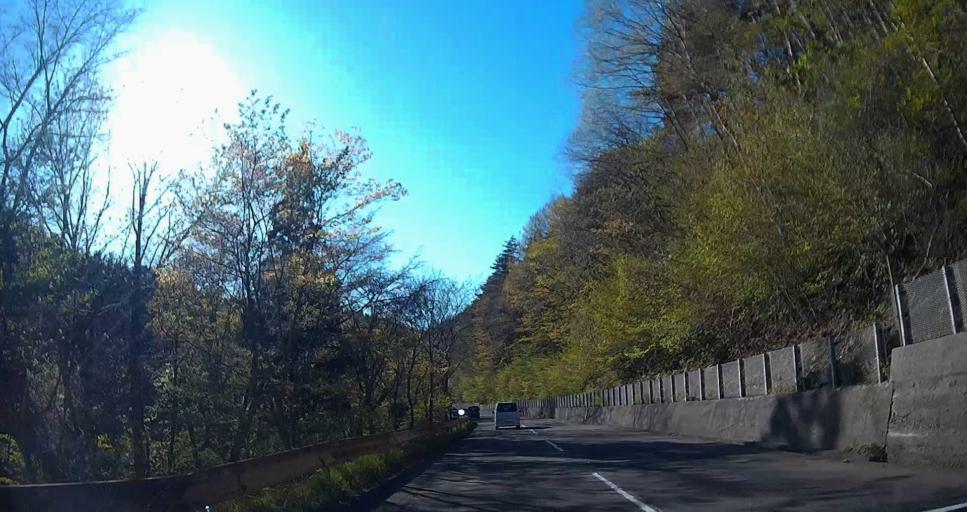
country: JP
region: Aomori
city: Mutsu
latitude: 41.4223
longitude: 141.1470
